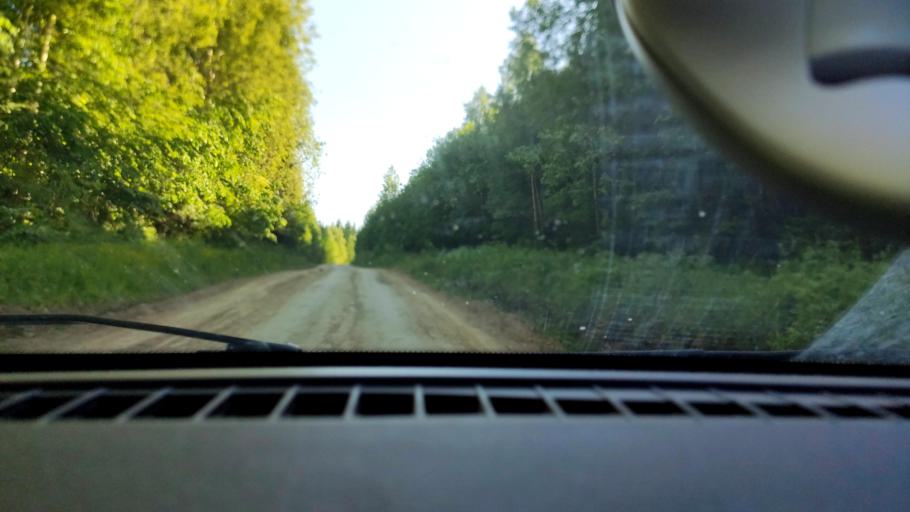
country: RU
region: Perm
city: Novyye Lyady
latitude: 58.1813
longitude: 56.5719
